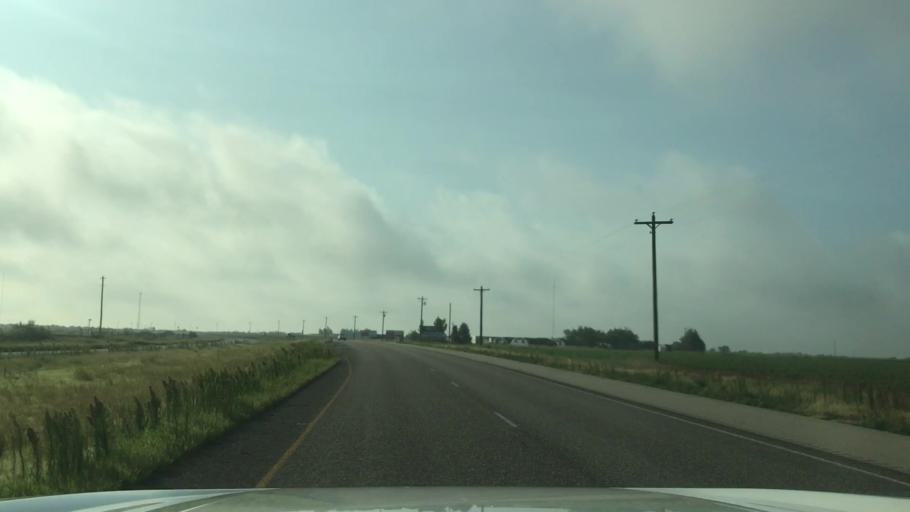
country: US
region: Texas
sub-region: Garza County
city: Post
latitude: 33.2188
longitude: -101.4355
